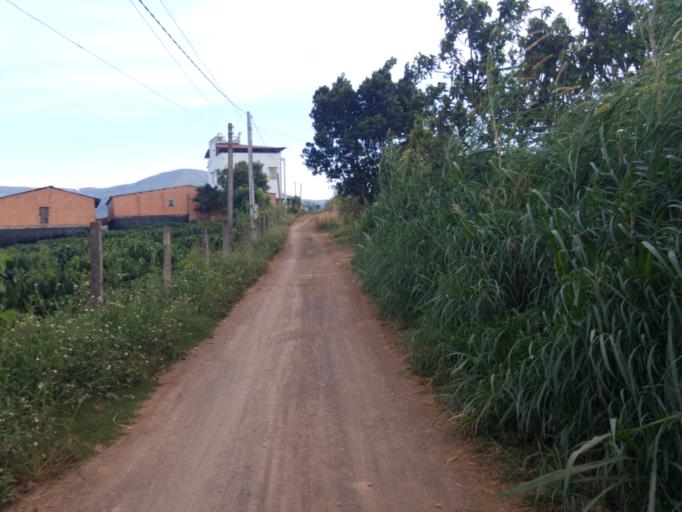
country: VN
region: Lam Dong
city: Duc Trong
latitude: 11.8387
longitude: 108.3477
